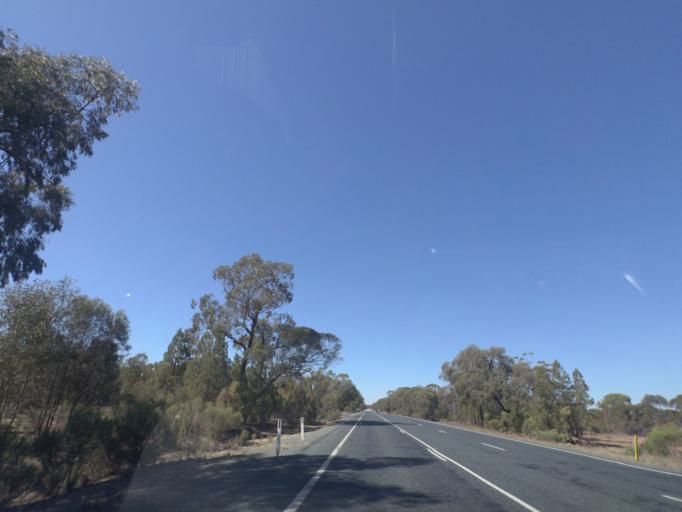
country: AU
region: New South Wales
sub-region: Bland
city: West Wyalong
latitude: -34.1300
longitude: 147.1239
